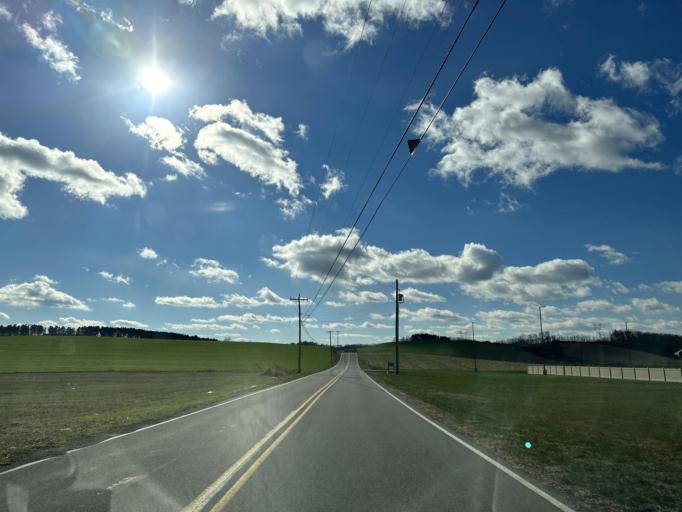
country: US
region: Pennsylvania
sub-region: Lebanon County
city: Richland
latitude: 40.4560
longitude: -76.2450
